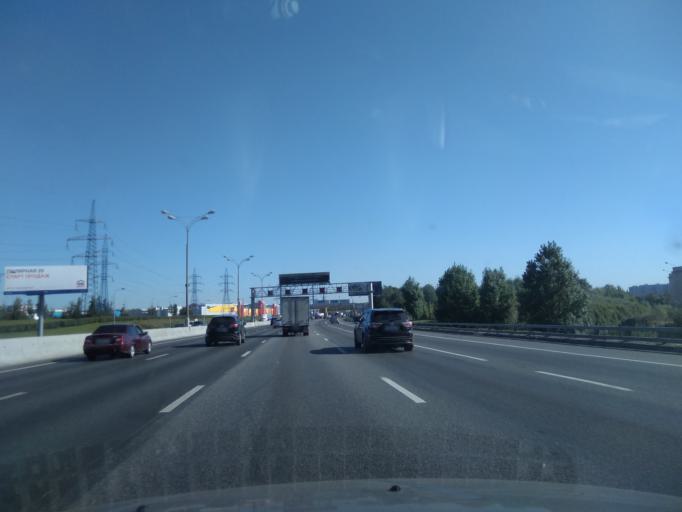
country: RU
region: Moscow
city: Lianozovo
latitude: 55.9106
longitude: 37.5713
